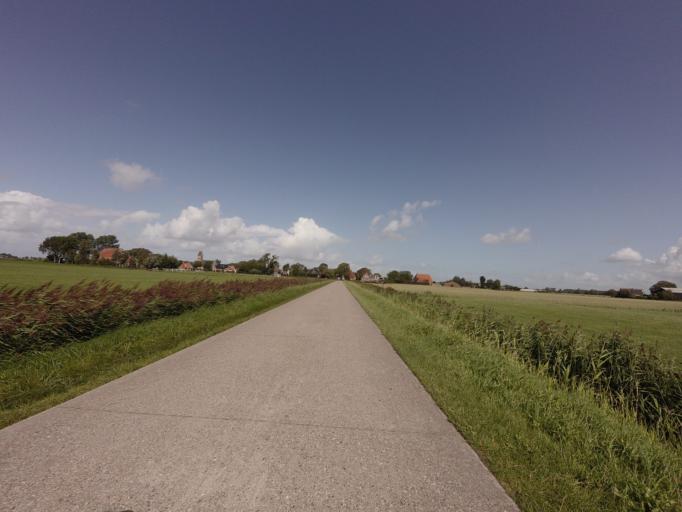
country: NL
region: Friesland
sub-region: Sudwest Fryslan
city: Makkum
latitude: 53.0773
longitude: 5.4526
